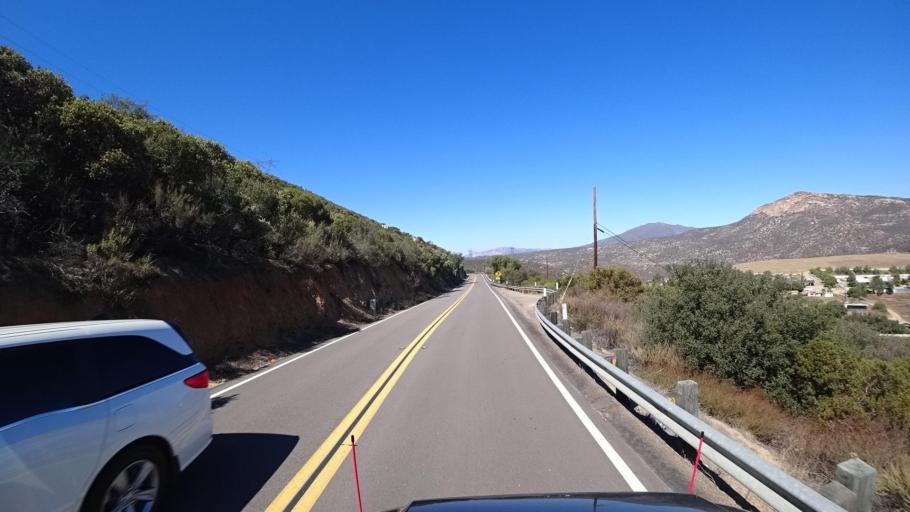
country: US
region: California
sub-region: San Diego County
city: Alpine
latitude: 32.7732
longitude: -116.7071
